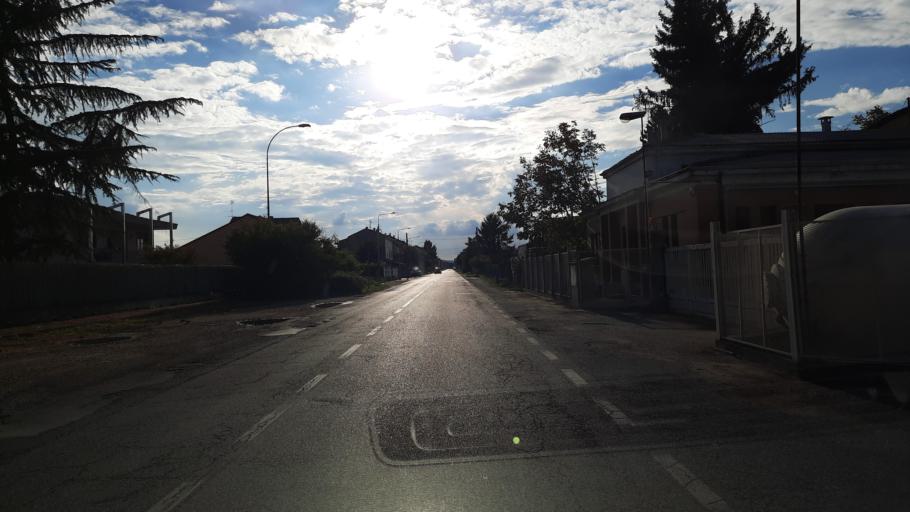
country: IT
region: Piedmont
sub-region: Provincia di Vercelli
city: Palazzolo Vercellese
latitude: 45.1883
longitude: 8.2408
